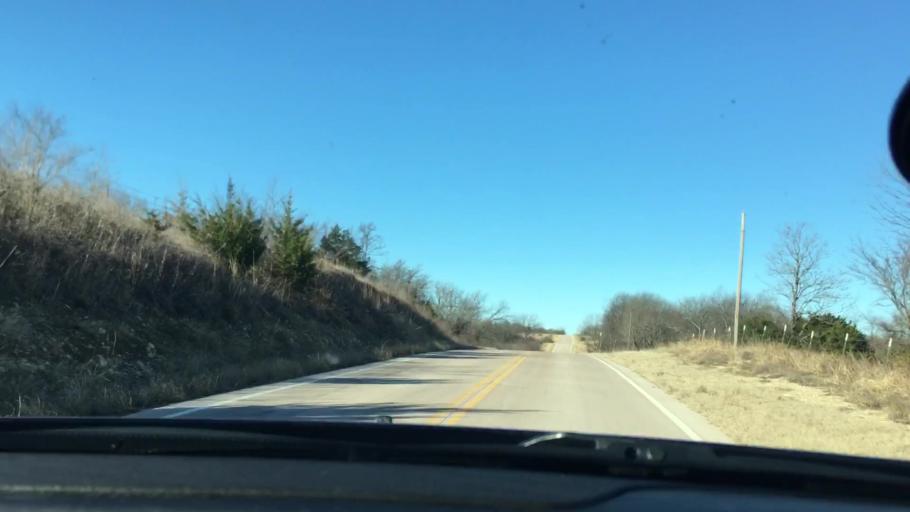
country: US
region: Oklahoma
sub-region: Johnston County
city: Tishomingo
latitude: 34.1144
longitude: -96.6367
